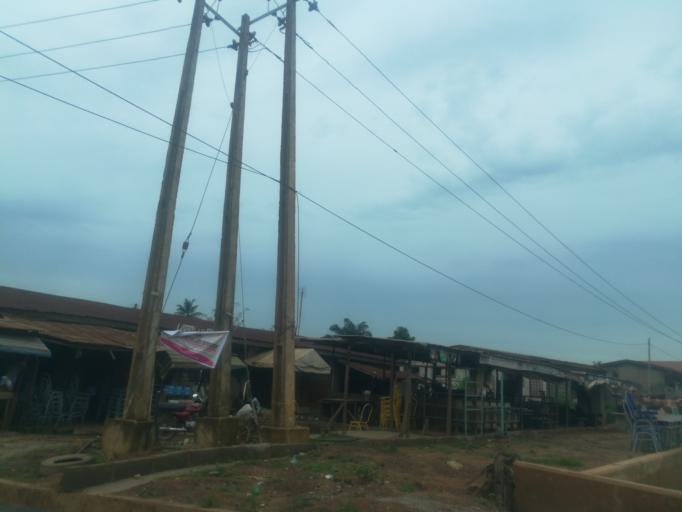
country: NG
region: Oyo
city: Ibadan
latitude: 7.3915
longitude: 3.9443
